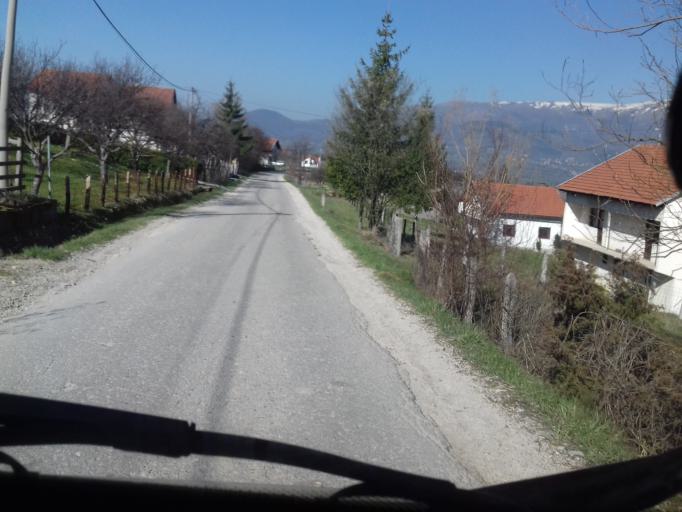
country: BA
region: Federation of Bosnia and Herzegovina
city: Lokvine
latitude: 44.2431
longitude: 17.7859
